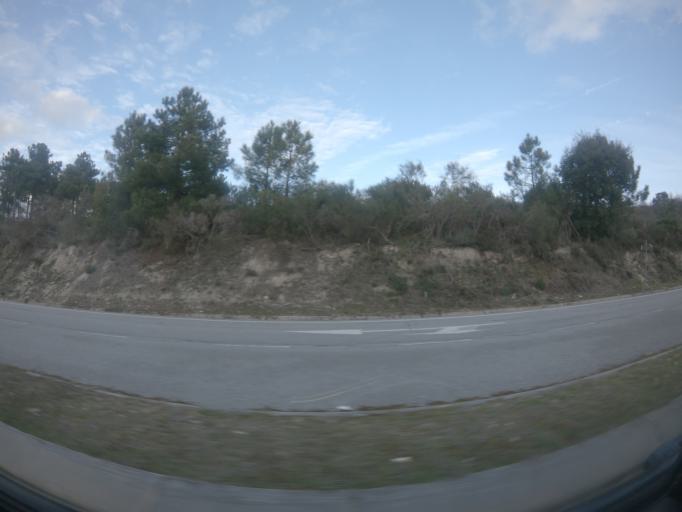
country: PT
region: Braganca
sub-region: Carrazeda de Ansiaes
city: Carrazeda de Anciaes
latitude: 41.2623
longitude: -7.3244
